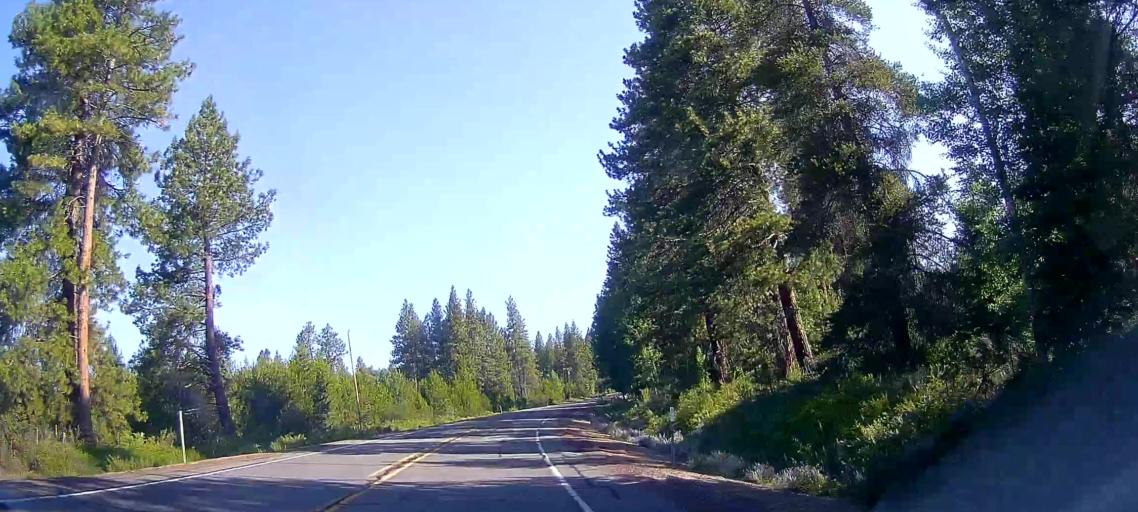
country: US
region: Oregon
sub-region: Klamath County
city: Klamath Falls
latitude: 42.6825
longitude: -121.9734
